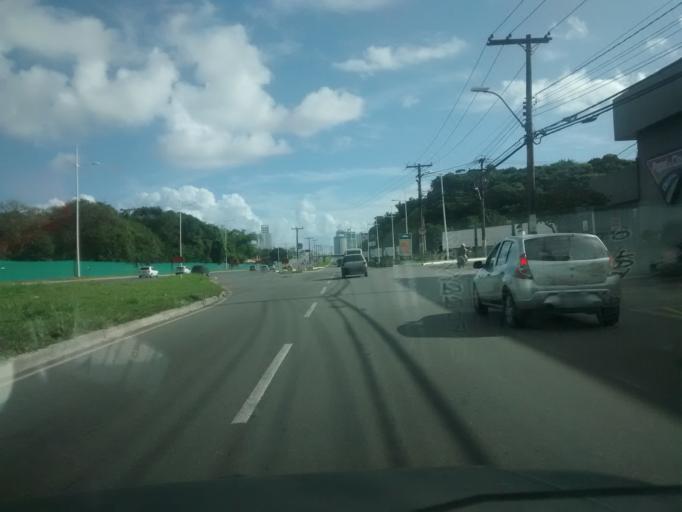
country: BR
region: Bahia
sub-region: Salvador
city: Salvador
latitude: -12.9691
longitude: -38.4424
